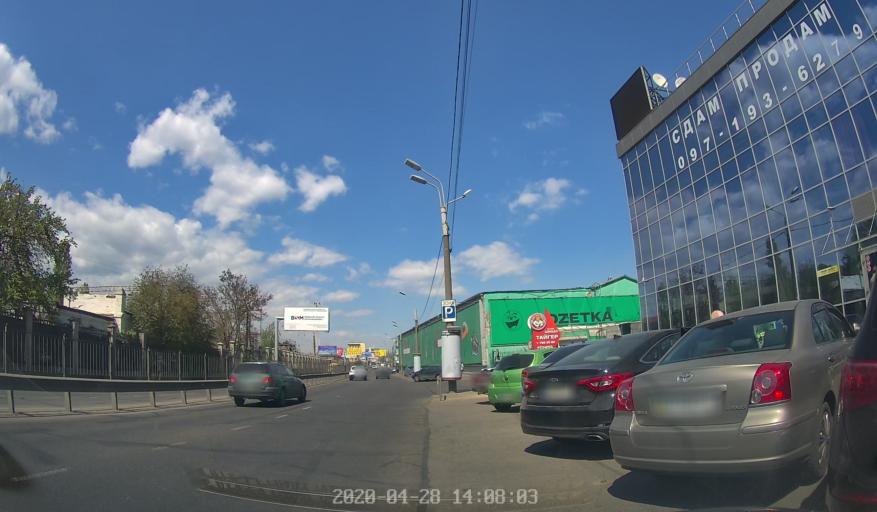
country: NG
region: Niger
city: Lemu
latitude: 9.2919
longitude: 6.1481
